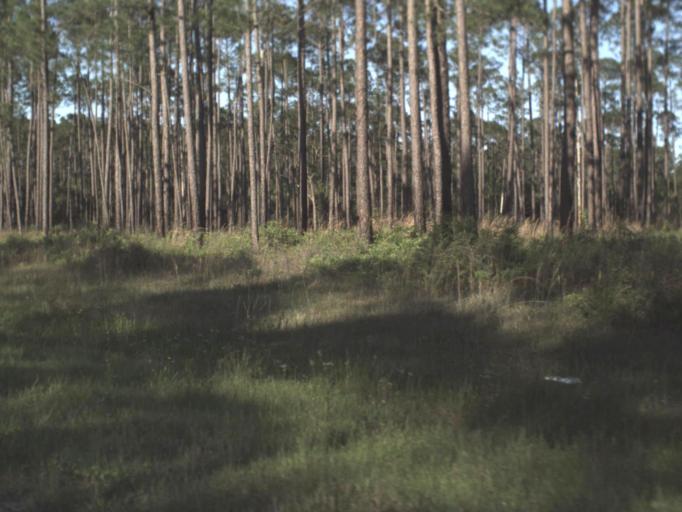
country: US
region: Florida
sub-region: Liberty County
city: Bristol
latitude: 30.3154
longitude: -84.8277
